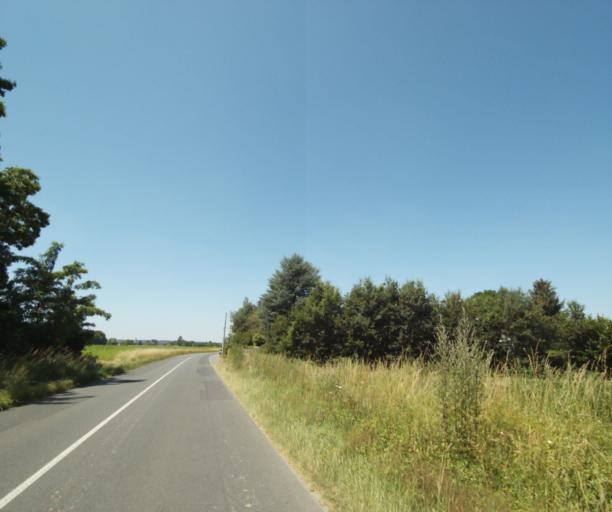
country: FR
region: Ile-de-France
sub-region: Departement de l'Essonne
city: Milly-la-Foret
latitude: 48.3925
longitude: 2.4877
